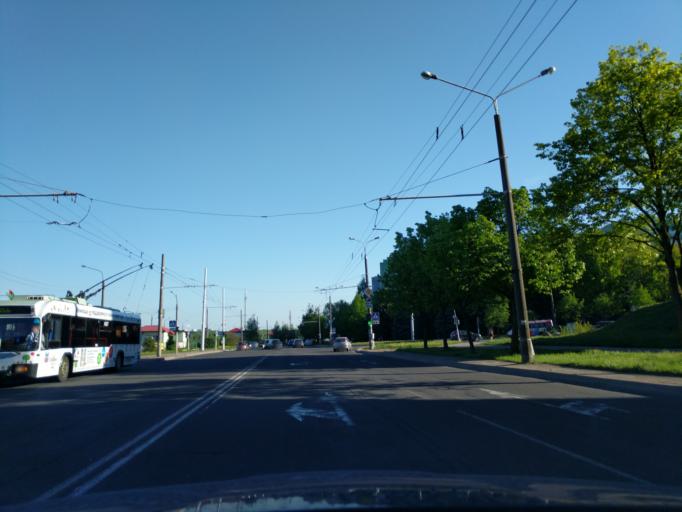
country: BY
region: Minsk
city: Novoye Medvezhino
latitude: 53.9046
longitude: 27.4629
